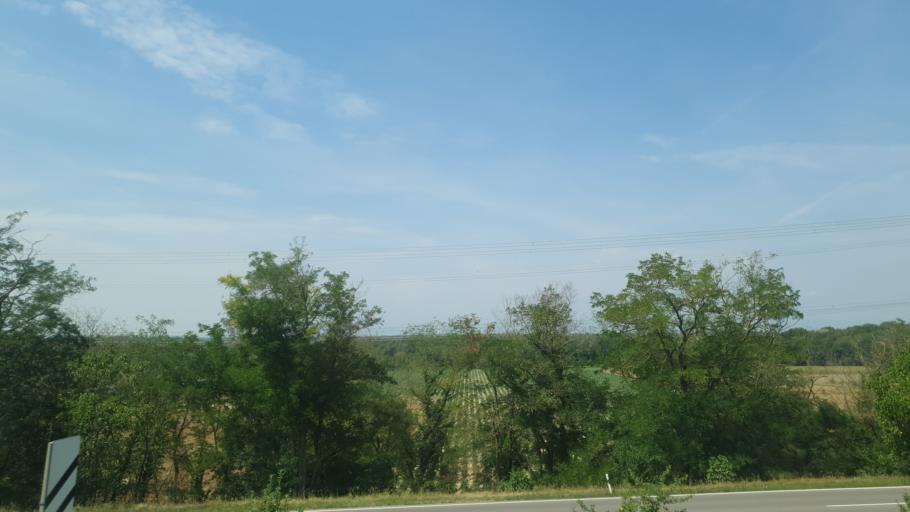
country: DE
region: Baden-Wuerttemberg
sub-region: Freiburg Region
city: Schliengen
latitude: 47.7497
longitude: 7.5618
